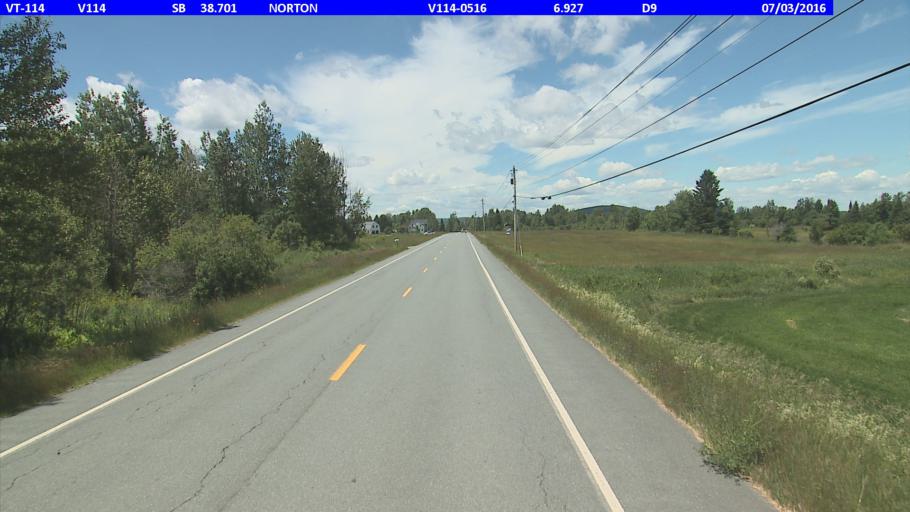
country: CA
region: Quebec
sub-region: Estrie
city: Coaticook
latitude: 45.0043
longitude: -71.7652
